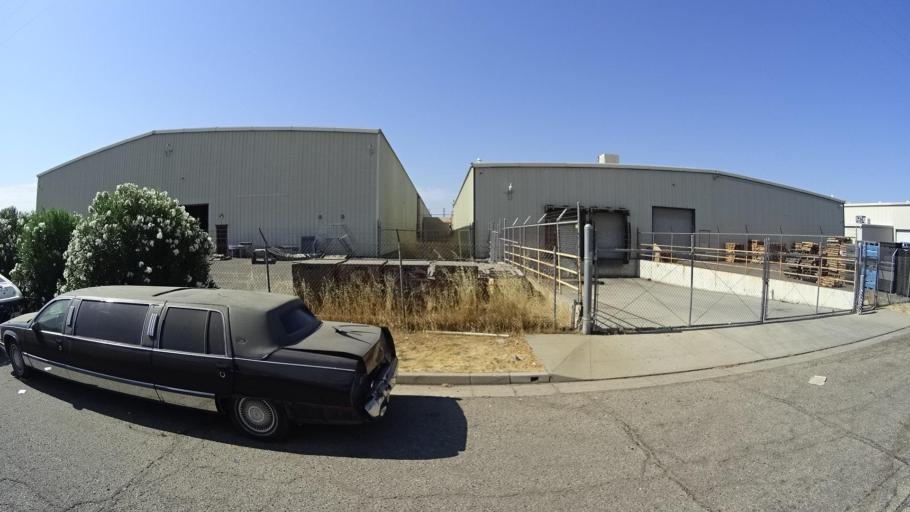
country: US
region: California
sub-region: Fresno County
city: Tarpey Village
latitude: 36.7830
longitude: -119.6952
